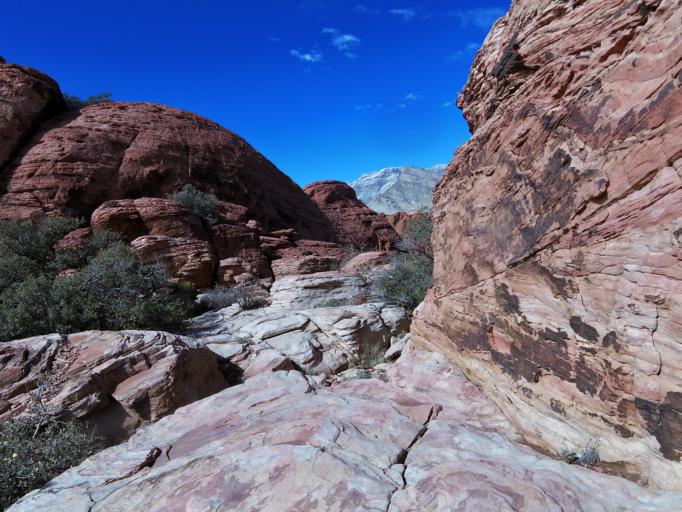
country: US
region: Nevada
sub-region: Clark County
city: Summerlin South
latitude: 36.1478
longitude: -115.4260
